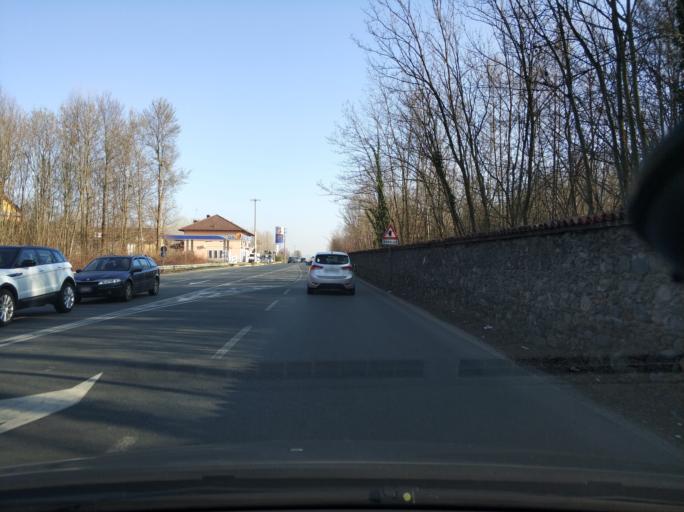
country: IT
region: Piedmont
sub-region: Provincia di Torino
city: Robassomero
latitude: 45.1943
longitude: 7.5622
